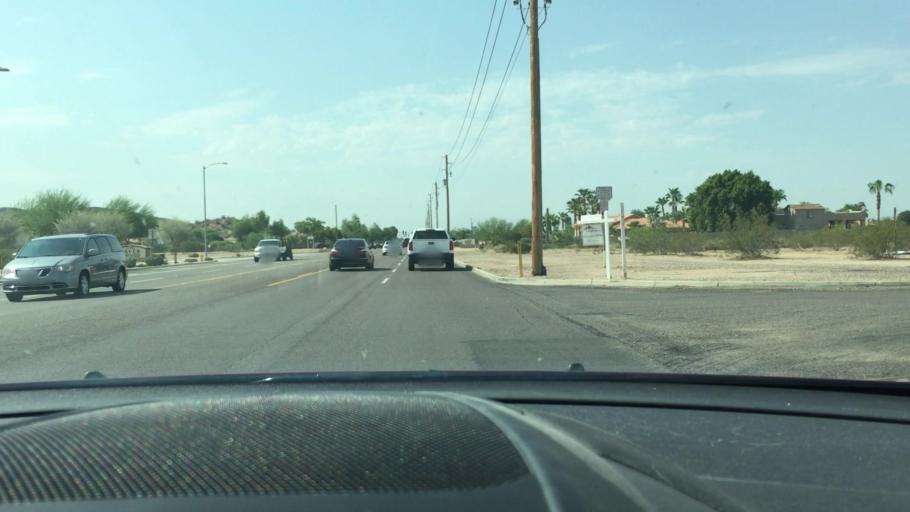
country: US
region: Arizona
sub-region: Maricopa County
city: Sun City
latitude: 33.6999
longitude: -112.2032
